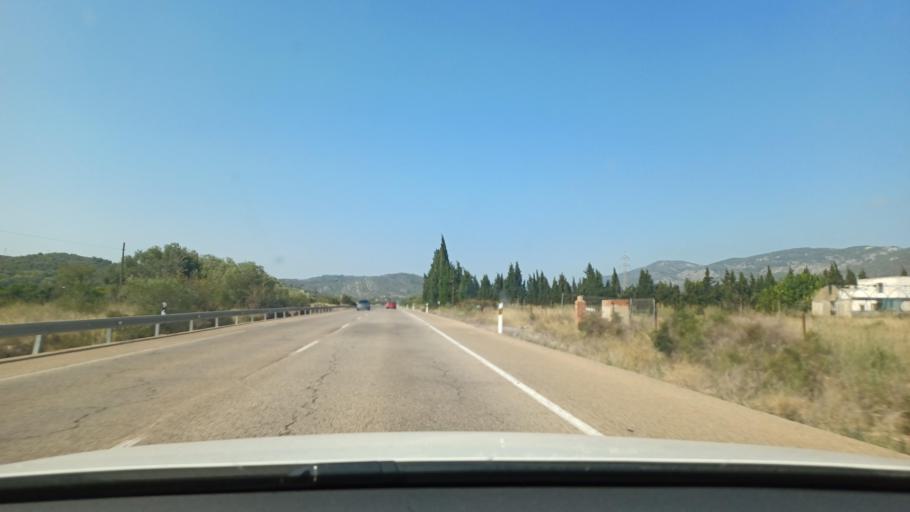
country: ES
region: Valencia
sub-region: Provincia de Castello
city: Alcala de Xivert
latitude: 40.2524
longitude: 0.2349
